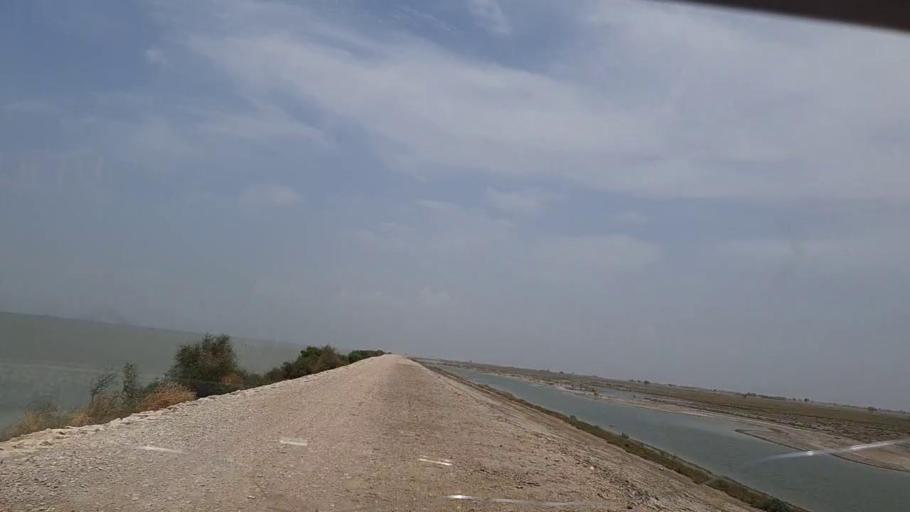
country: PK
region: Sindh
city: Sehwan
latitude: 26.4186
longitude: 67.7391
